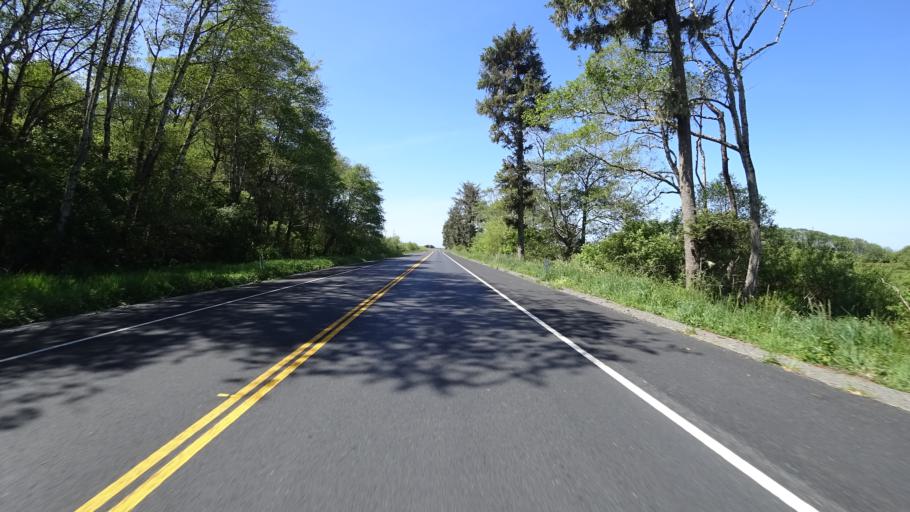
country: US
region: California
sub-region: Humboldt County
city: Westhaven-Moonstone
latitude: 41.2864
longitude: -124.0860
